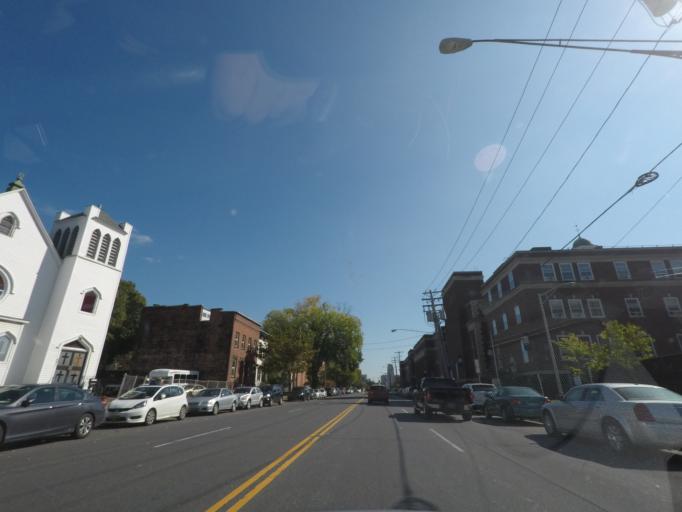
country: US
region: New York
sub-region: Albany County
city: Albany
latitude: 42.6620
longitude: -73.7725
